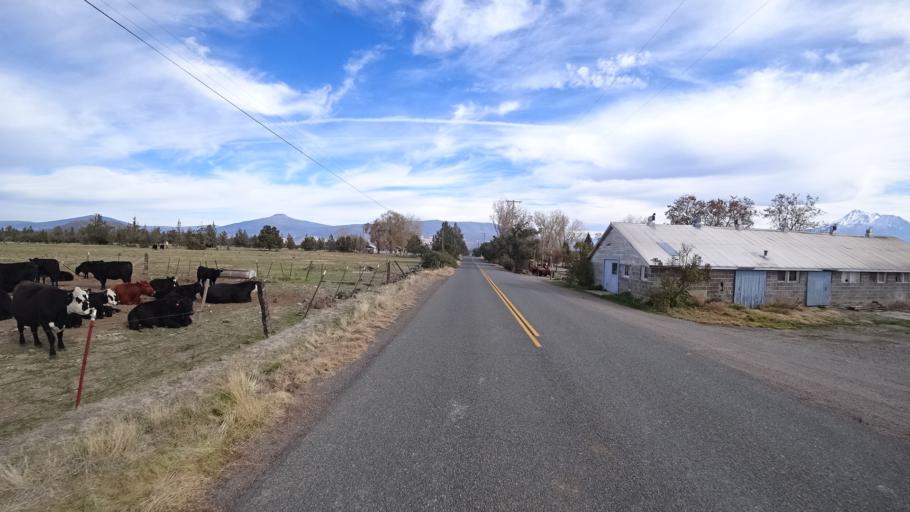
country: US
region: California
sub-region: Siskiyou County
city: Montague
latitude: 41.6385
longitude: -122.4209
